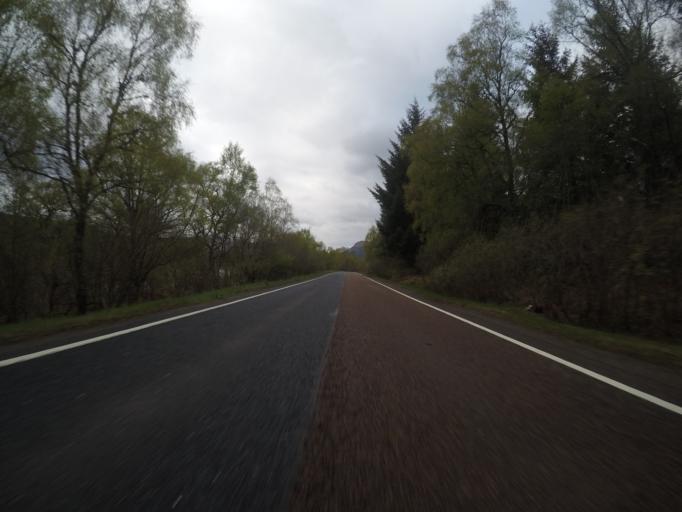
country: GB
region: Scotland
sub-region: Highland
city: Kingussie
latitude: 56.9690
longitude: -4.4382
